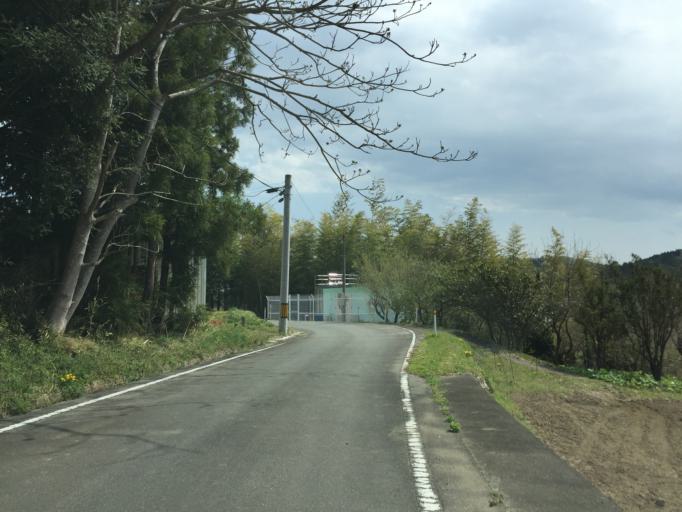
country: JP
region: Fukushima
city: Iwaki
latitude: 37.1651
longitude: 140.9744
